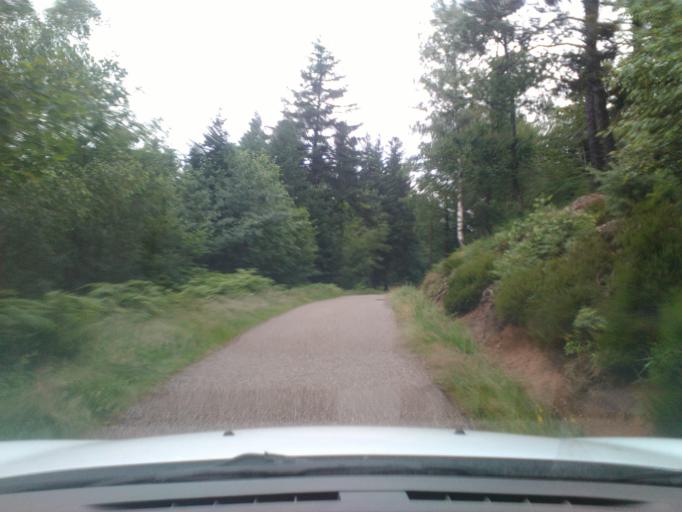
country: FR
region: Lorraine
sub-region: Departement des Vosges
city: Le Tholy
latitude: 48.1084
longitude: 6.7049
